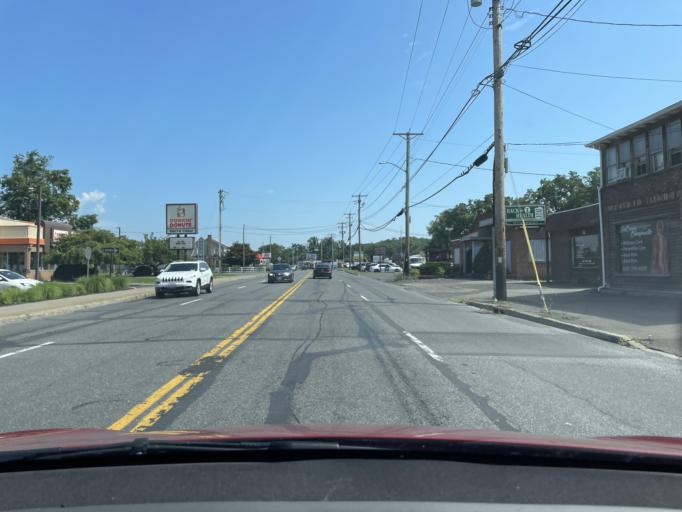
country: US
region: New York
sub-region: Ulster County
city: Lincoln Park
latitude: 41.9446
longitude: -73.9963
